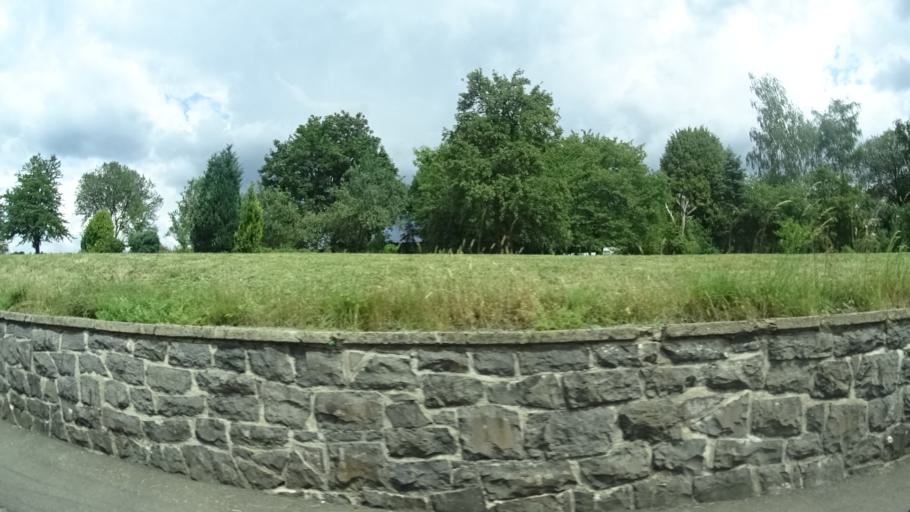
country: DE
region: Hesse
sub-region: Regierungsbezirk Giessen
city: Grebenhain
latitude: 50.4480
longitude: 9.2784
